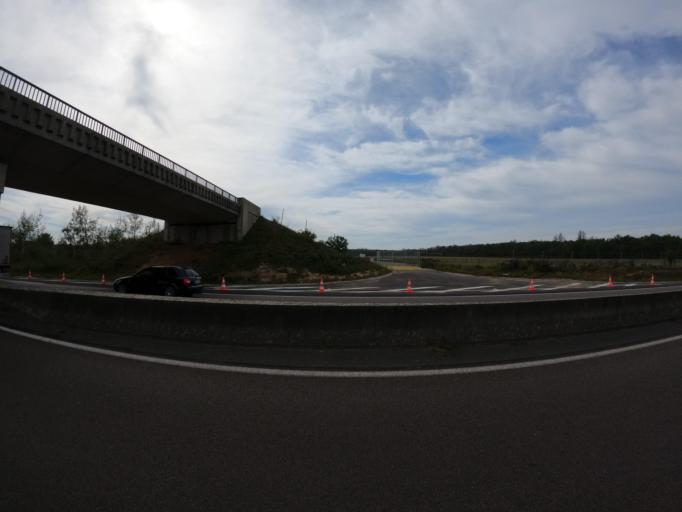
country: FR
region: Bourgogne
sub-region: Departement de Saone-et-Loire
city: Digoin
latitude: 46.4707
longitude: 4.0320
